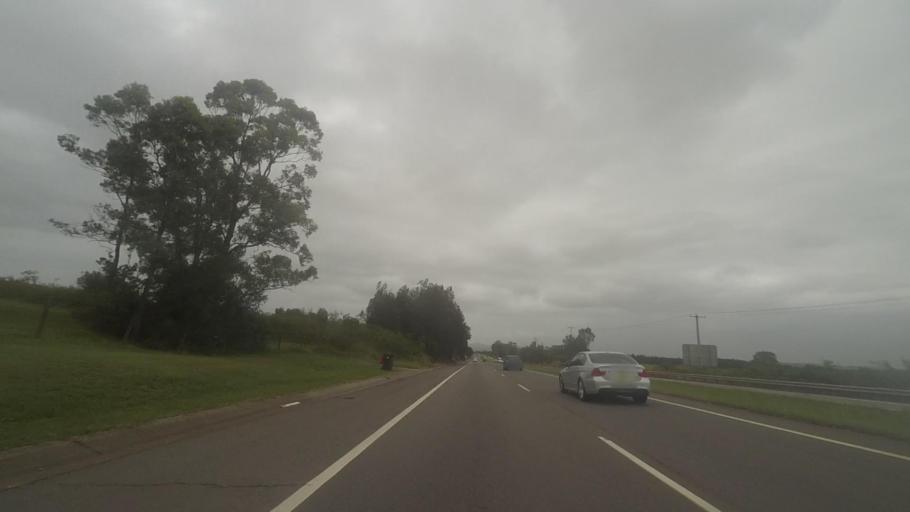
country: AU
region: New South Wales
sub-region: Newcastle
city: Beresfield
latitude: -32.8123
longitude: 151.7053
